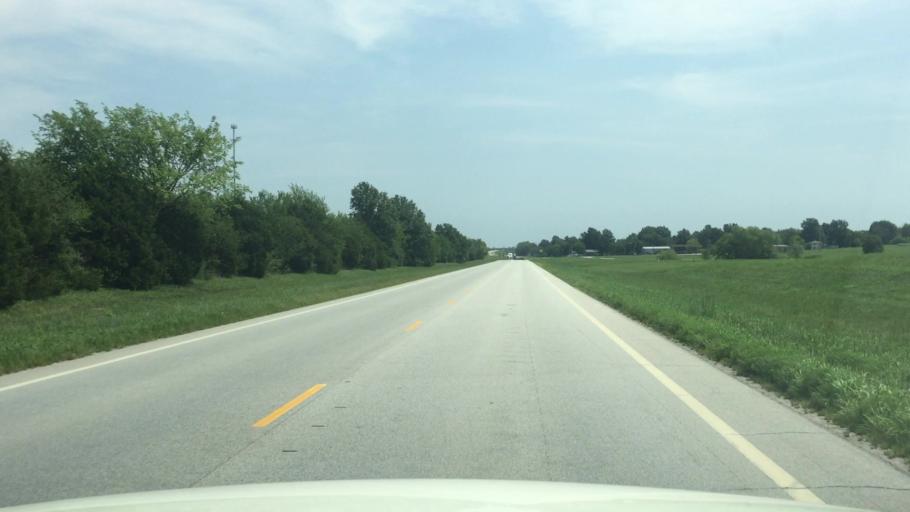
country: US
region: Kansas
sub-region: Cherokee County
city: Columbus
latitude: 37.1786
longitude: -94.8569
